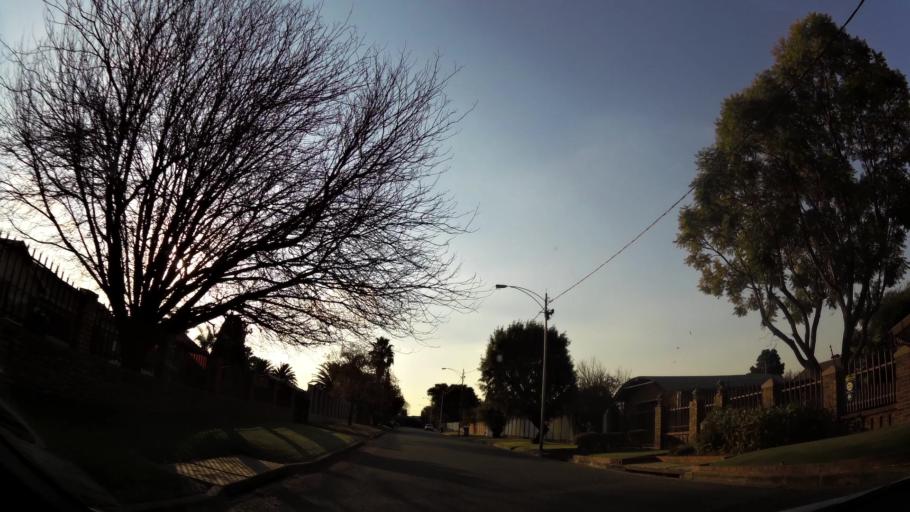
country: ZA
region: Gauteng
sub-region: Ekurhuleni Metropolitan Municipality
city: Springs
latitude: -26.2583
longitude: 28.3992
